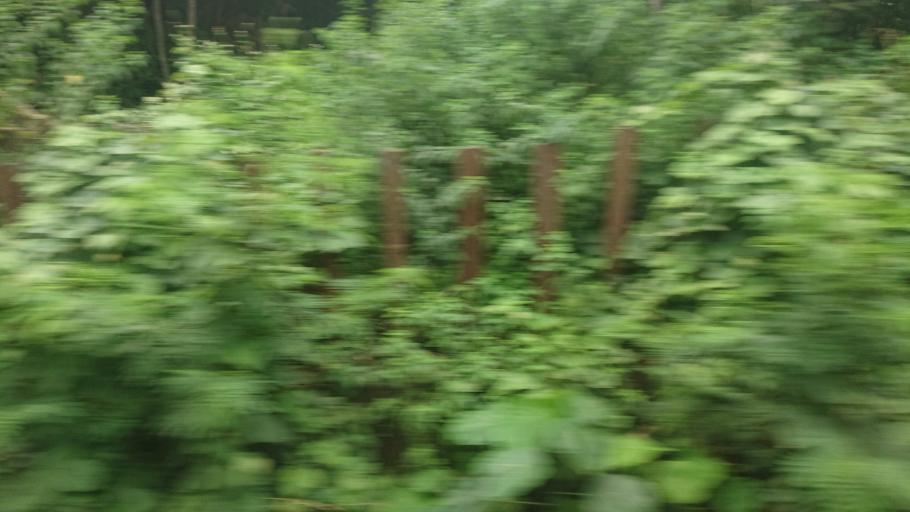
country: TW
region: Taiwan
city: Lugu
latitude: 23.8231
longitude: 120.8343
